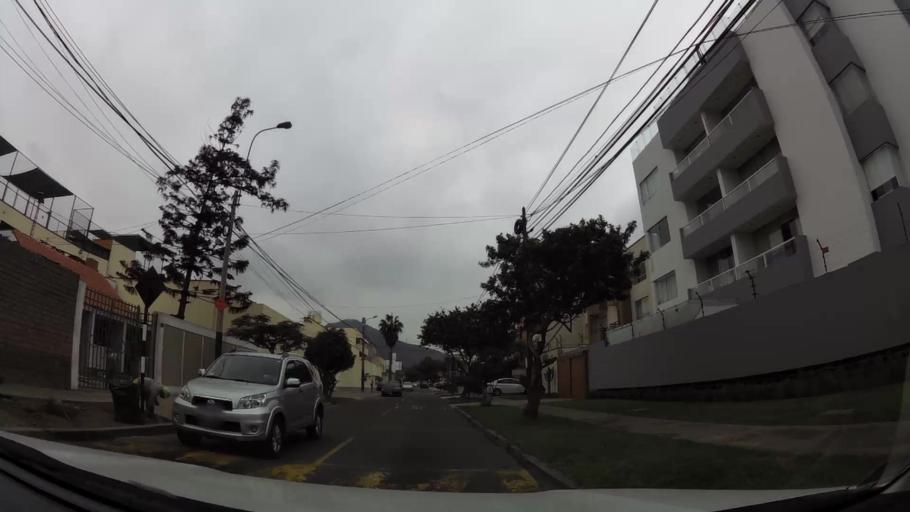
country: PE
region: Lima
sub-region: Lima
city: La Molina
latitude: -12.1107
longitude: -76.9709
